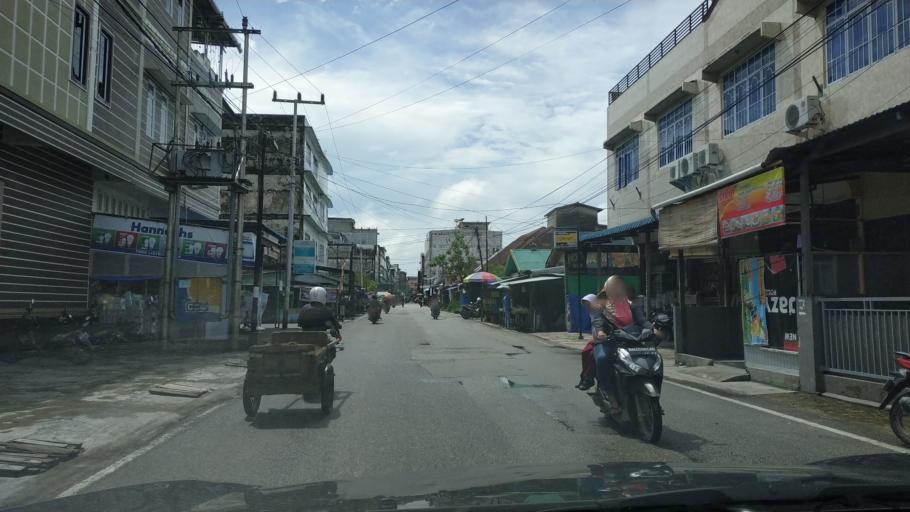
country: ID
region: Riau
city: Tembilahan
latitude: -0.3245
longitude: 103.1558
